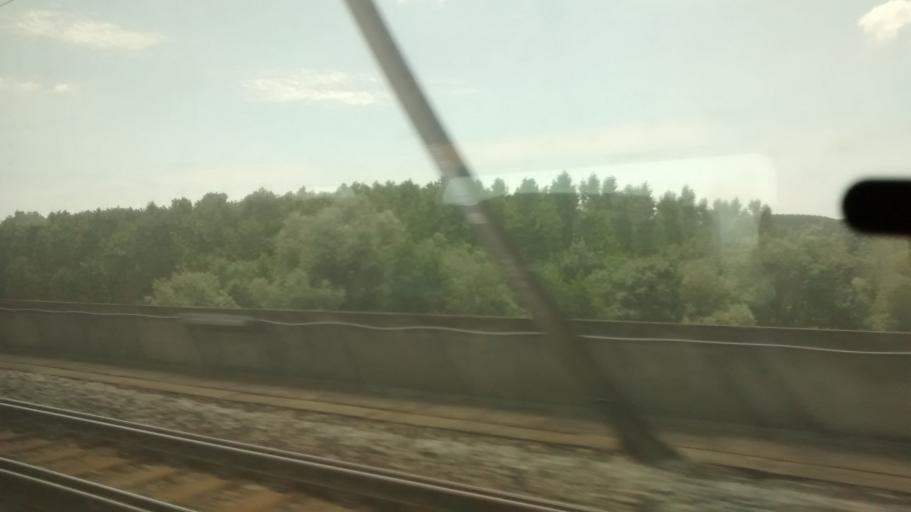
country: FR
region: Bourgogne
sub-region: Departement de Saone-et-Loire
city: Creches-sur-Saone
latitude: 46.2625
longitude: 4.8158
